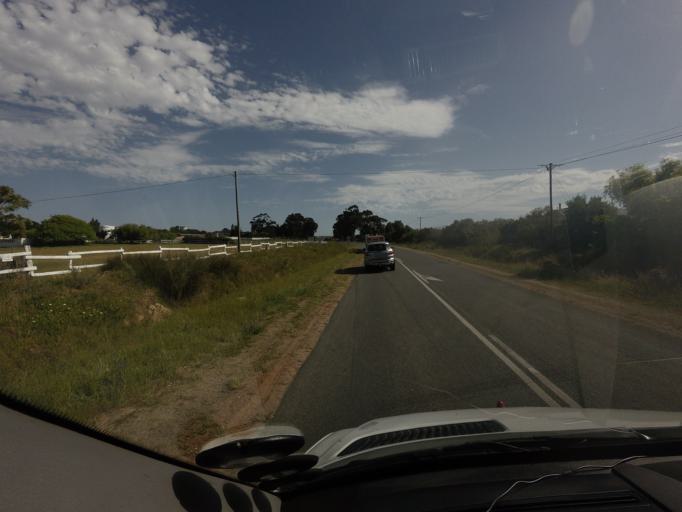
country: ZA
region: Western Cape
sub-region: Overberg District Municipality
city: Caledon
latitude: -34.4360
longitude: 19.4621
